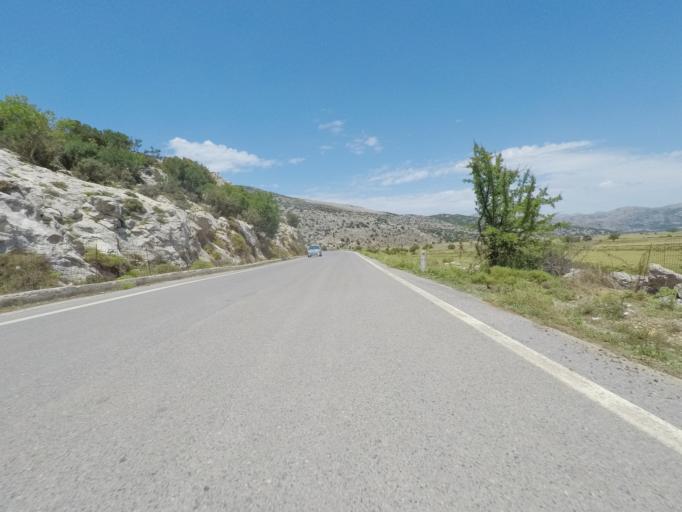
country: GR
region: Crete
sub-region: Nomos Irakleiou
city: Mokhos
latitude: 35.1888
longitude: 25.4314
